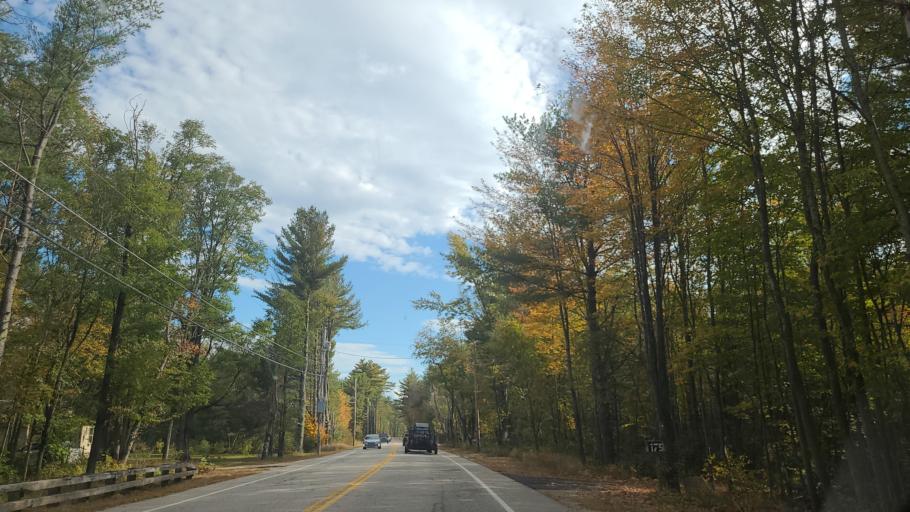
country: US
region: New Hampshire
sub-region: Carroll County
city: North Conway
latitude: 44.0249
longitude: -71.1327
